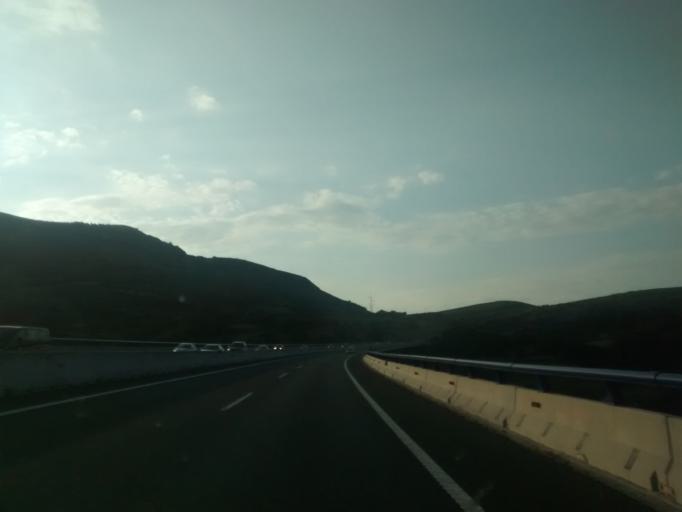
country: ES
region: Cantabria
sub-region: Provincia de Cantabria
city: Arenas de Iguna
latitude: 43.1925
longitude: -4.0696
